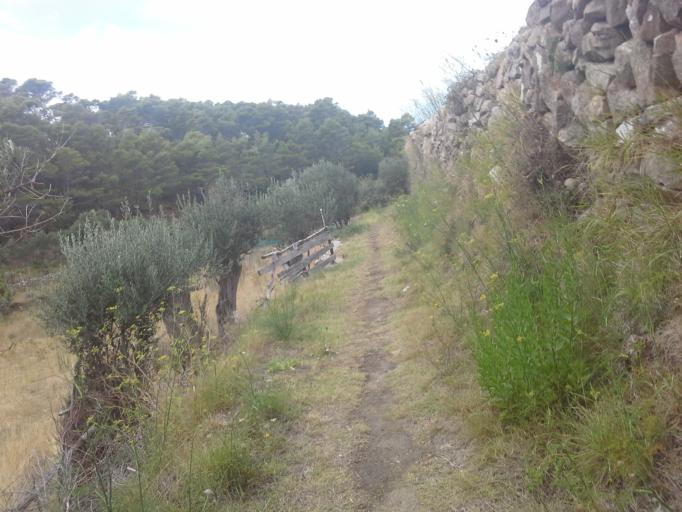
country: HR
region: Primorsko-Goranska
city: Banjol
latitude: 44.7563
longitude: 14.7755
